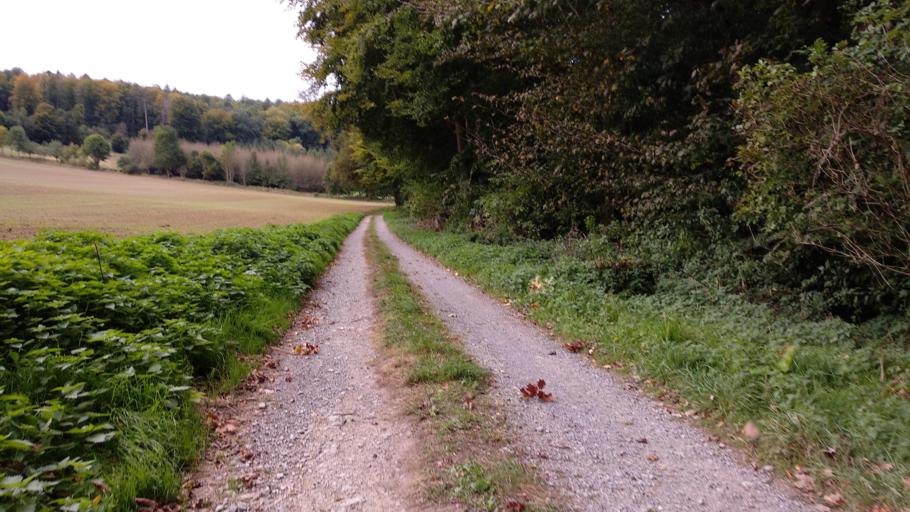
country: DE
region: North Rhine-Westphalia
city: Beverungen
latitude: 51.6926
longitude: 9.3688
